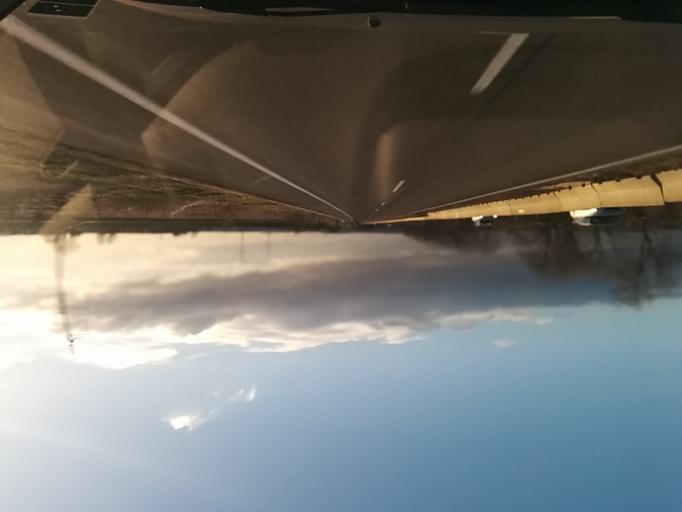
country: SK
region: Trnavsky
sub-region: Okres Trnava
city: Trnava
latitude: 48.3559
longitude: 17.6678
